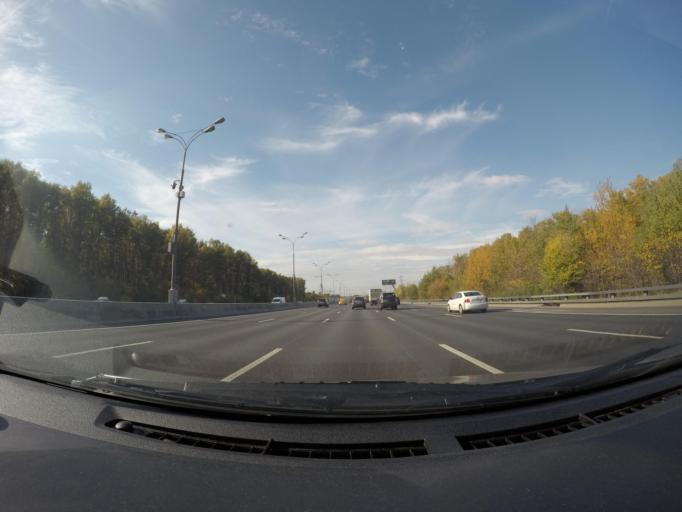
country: RU
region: Moscow
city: Vatutino
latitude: 55.8965
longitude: 37.6524
